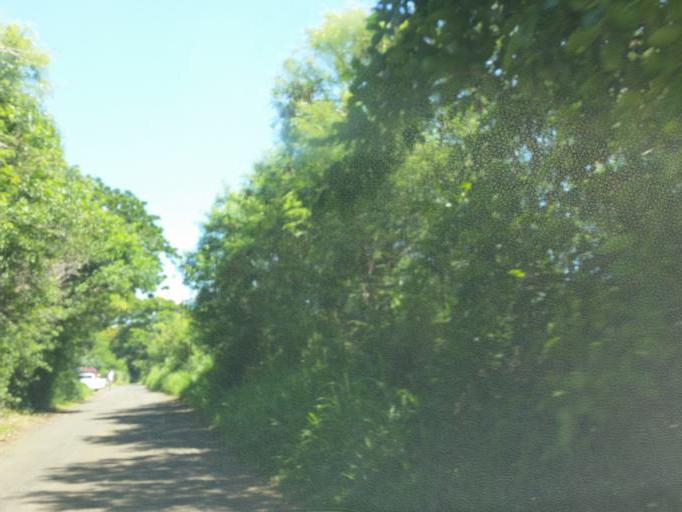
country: RE
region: Reunion
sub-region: Reunion
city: Sainte-Marie
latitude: -20.9087
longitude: 55.5167
